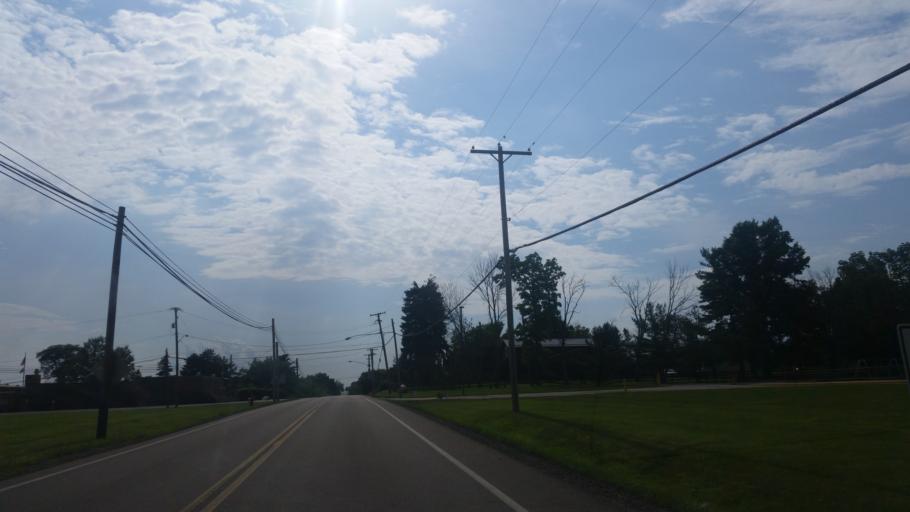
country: US
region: Ohio
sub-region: Summit County
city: Richfield
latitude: 41.2025
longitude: -81.6147
